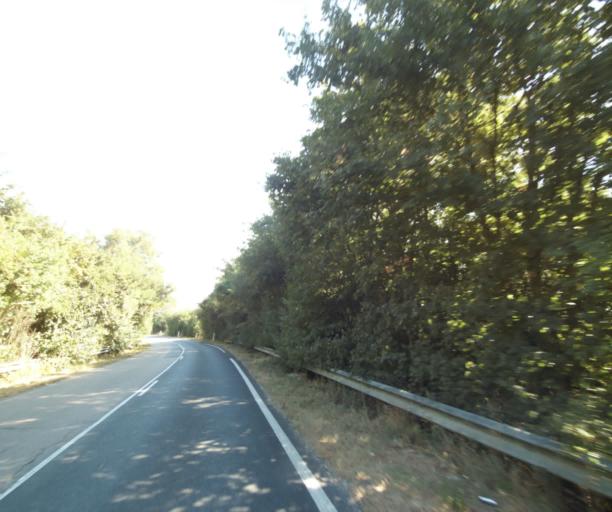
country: FR
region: Ile-de-France
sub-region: Departement de Seine-et-Marne
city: Moissy-Cramayel
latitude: 48.6063
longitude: 2.5889
